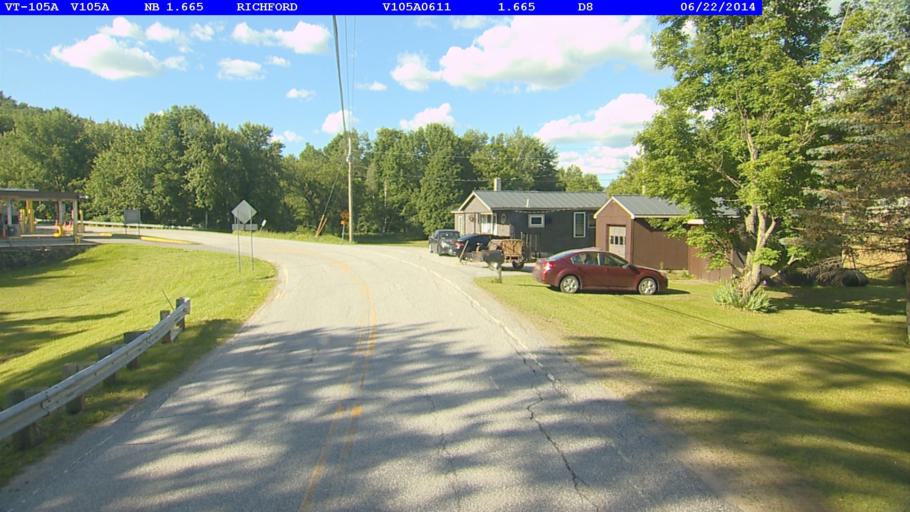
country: US
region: Vermont
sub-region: Franklin County
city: Richford
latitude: 45.0105
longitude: -72.5875
